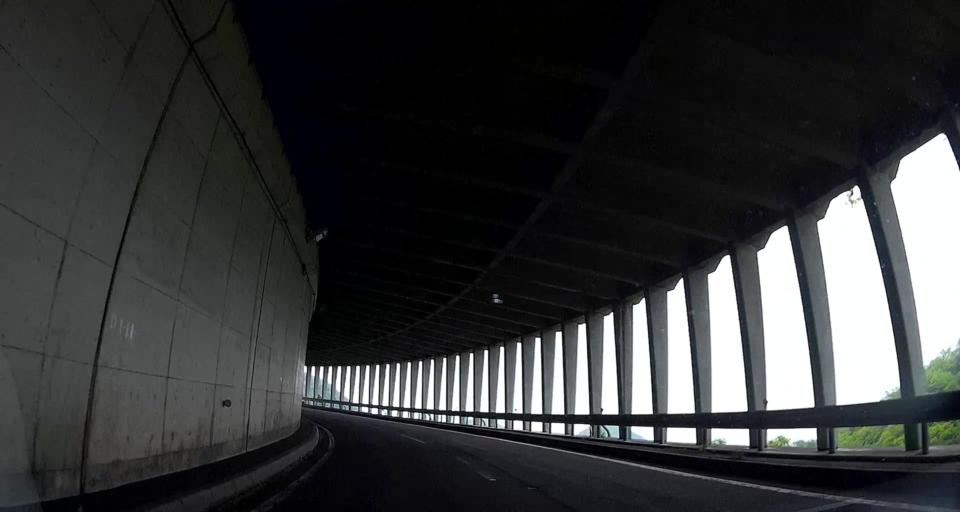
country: JP
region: Hokkaido
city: Shiraoi
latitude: 42.6583
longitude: 141.1745
